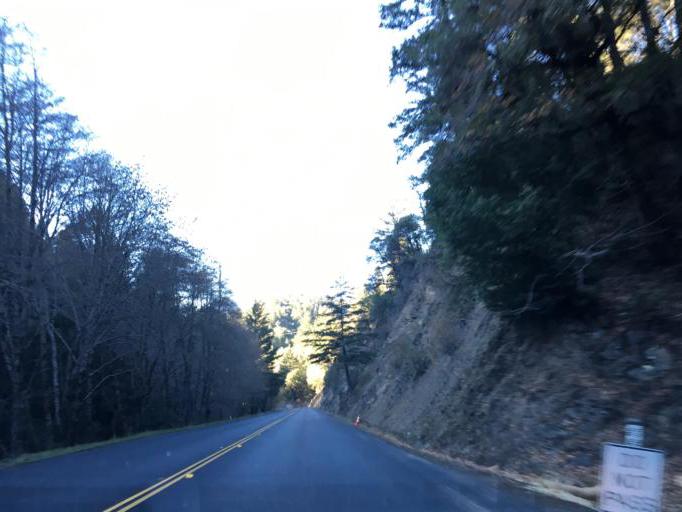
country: US
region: California
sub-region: Mendocino County
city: Laytonville
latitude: 39.8251
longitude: -123.5679
